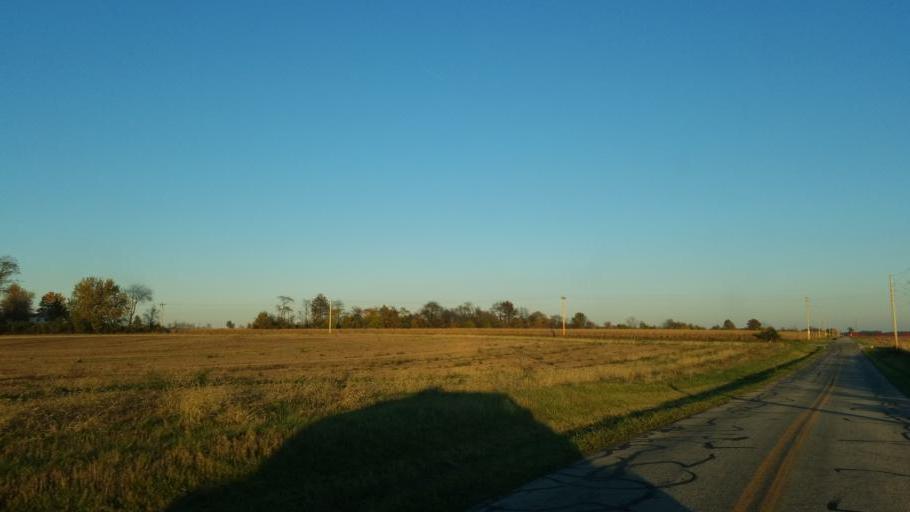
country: US
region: Ohio
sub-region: Huron County
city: Bellevue
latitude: 41.2118
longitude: -82.8813
